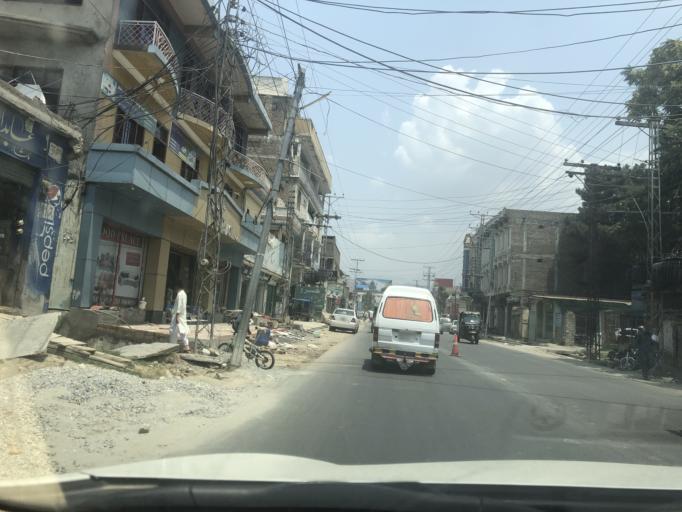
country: PK
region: Khyber Pakhtunkhwa
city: Mingora
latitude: 34.7691
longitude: 72.3366
